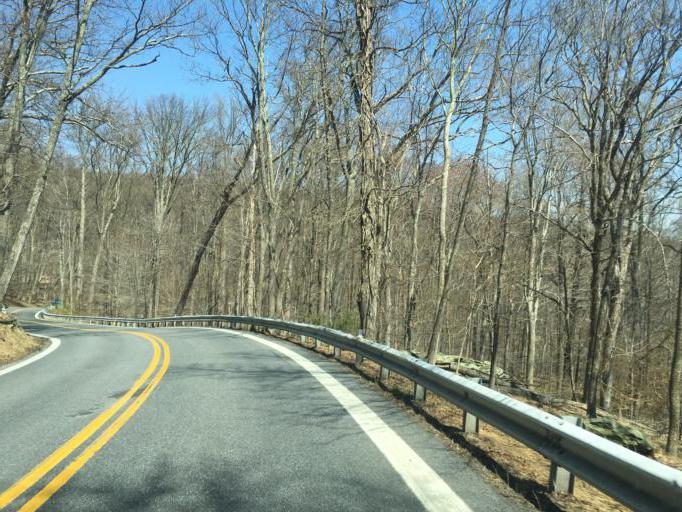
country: US
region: Maryland
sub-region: Frederick County
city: Thurmont
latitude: 39.6327
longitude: -77.4708
